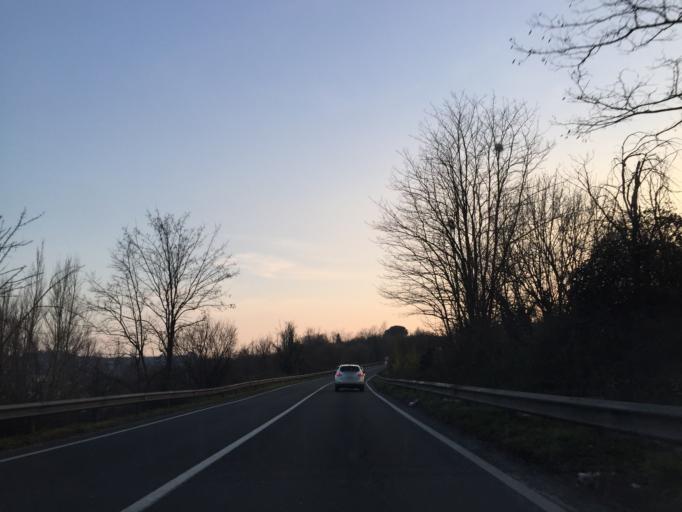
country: IT
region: Campania
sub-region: Provincia di Avellino
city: Avellino
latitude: 40.9068
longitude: 14.8096
